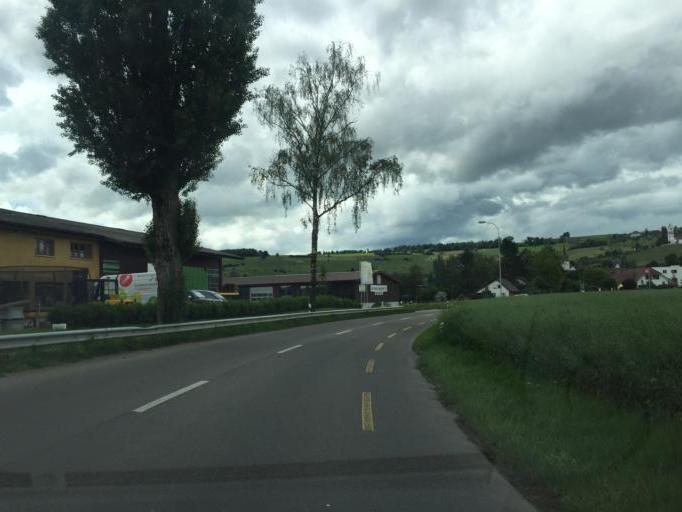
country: CH
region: Schaffhausen
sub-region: Bezirk Unterklettgau
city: Hallau
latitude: 47.6935
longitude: 8.4668
